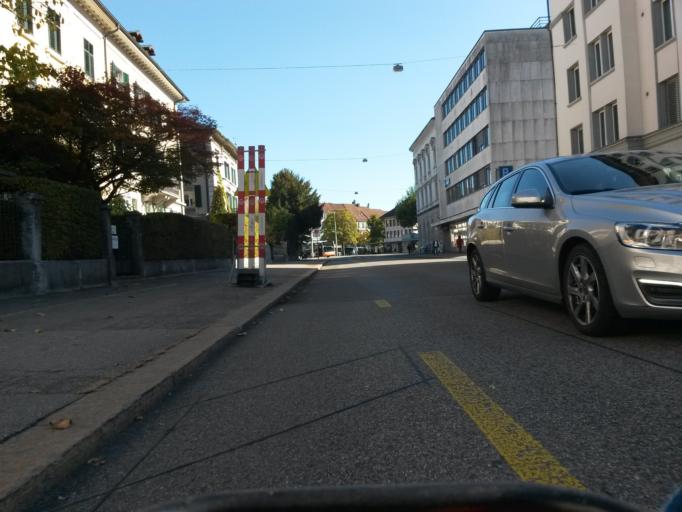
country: CH
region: Solothurn
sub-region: Bezirk Solothurn
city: Solothurn
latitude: 47.2087
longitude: 7.5327
